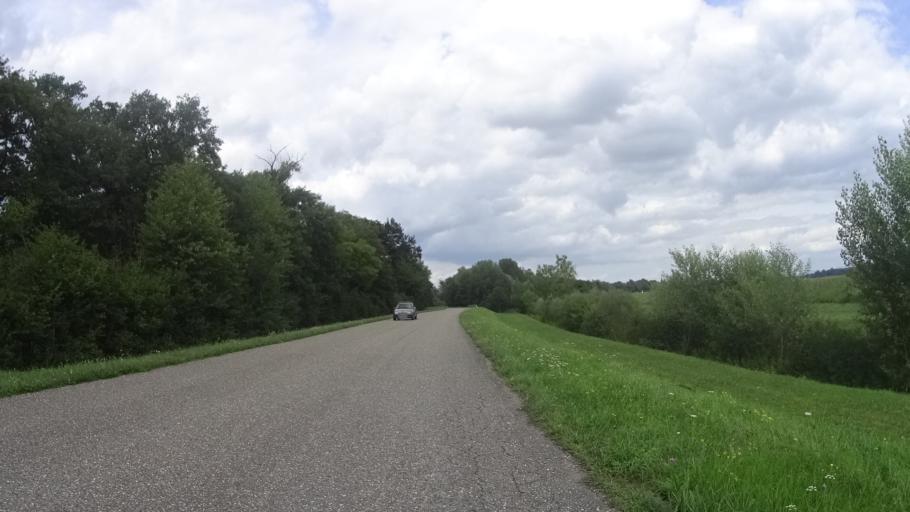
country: FR
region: Alsace
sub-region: Departement du Bas-Rhin
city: Drusenheim
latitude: 48.7581
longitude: 7.9691
